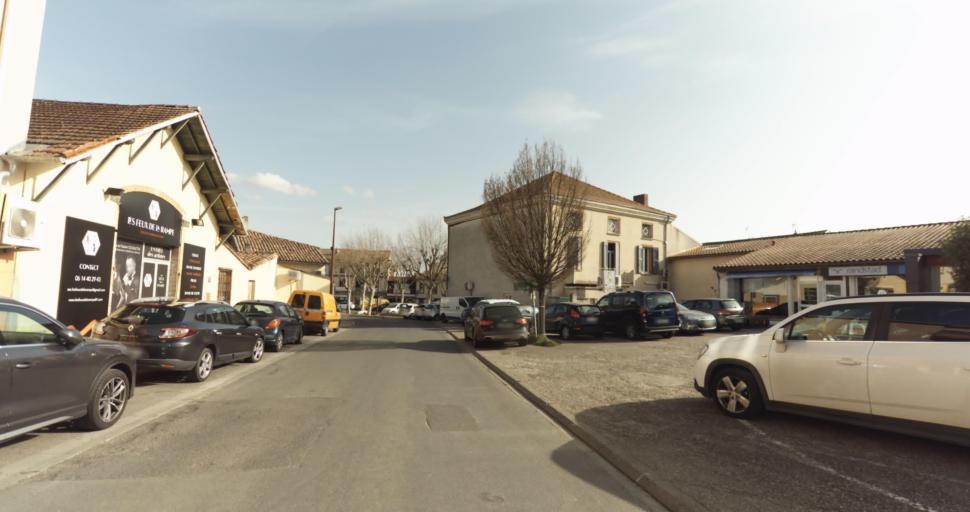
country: FR
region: Midi-Pyrenees
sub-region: Departement du Tarn
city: Saint-Sulpice-la-Pointe
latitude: 43.7725
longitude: 1.6869
